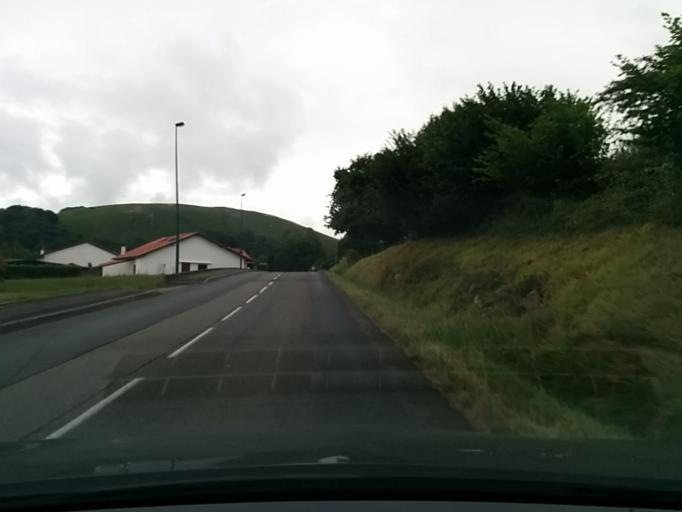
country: FR
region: Aquitaine
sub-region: Departement des Pyrenees-Atlantiques
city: Saint-Pee-sur-Nivelle
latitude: 43.3332
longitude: -1.5480
